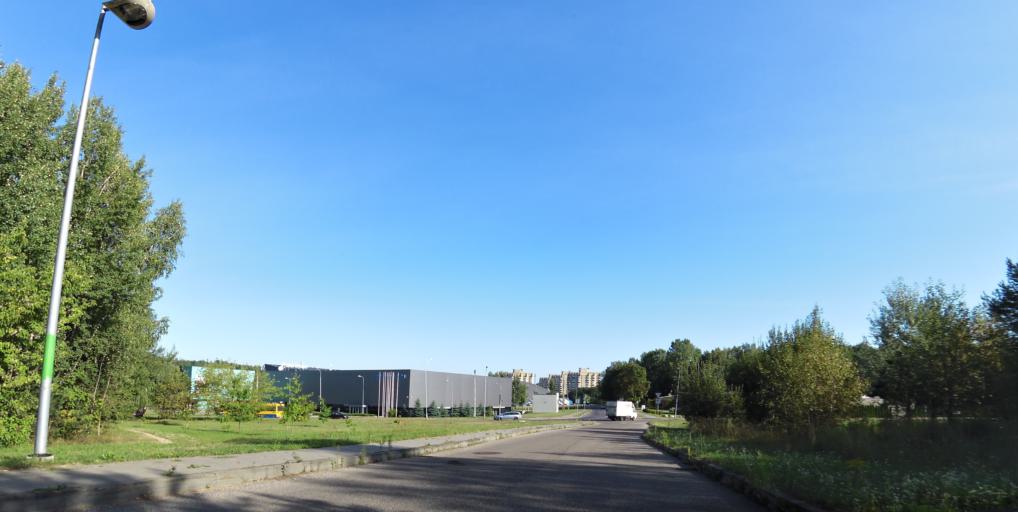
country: LT
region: Vilnius County
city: Seskine
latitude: 54.7040
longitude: 25.2376
